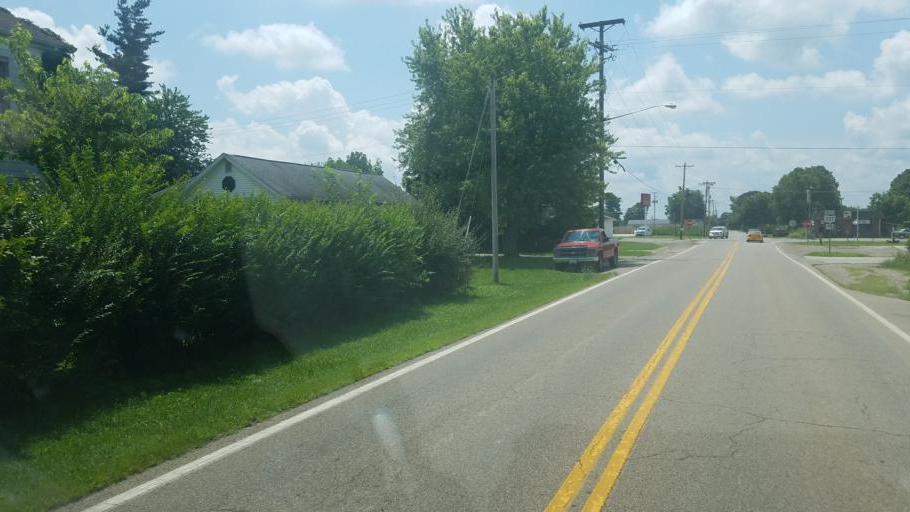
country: US
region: Ohio
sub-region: Ross County
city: Chillicothe
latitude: 39.2676
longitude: -82.7901
